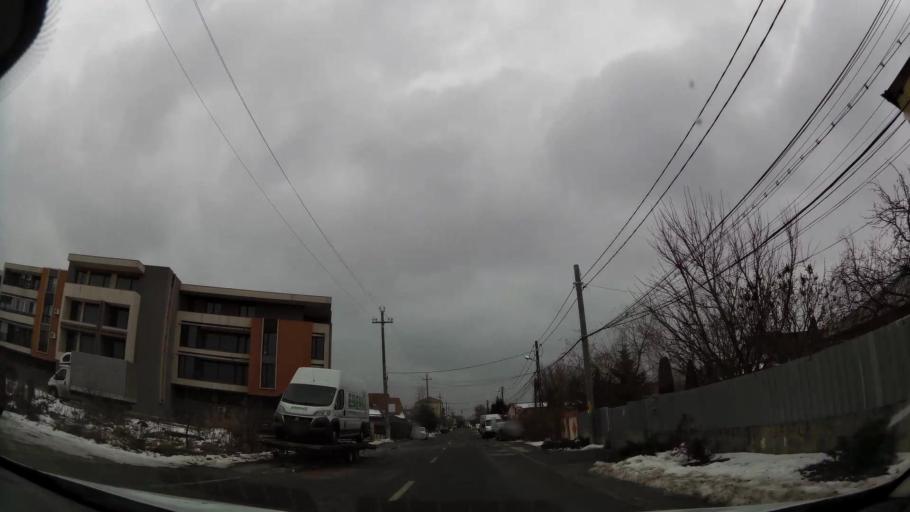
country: RO
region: Ilfov
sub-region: Comuna Otopeni
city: Otopeni
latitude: 44.5546
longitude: 26.0800
